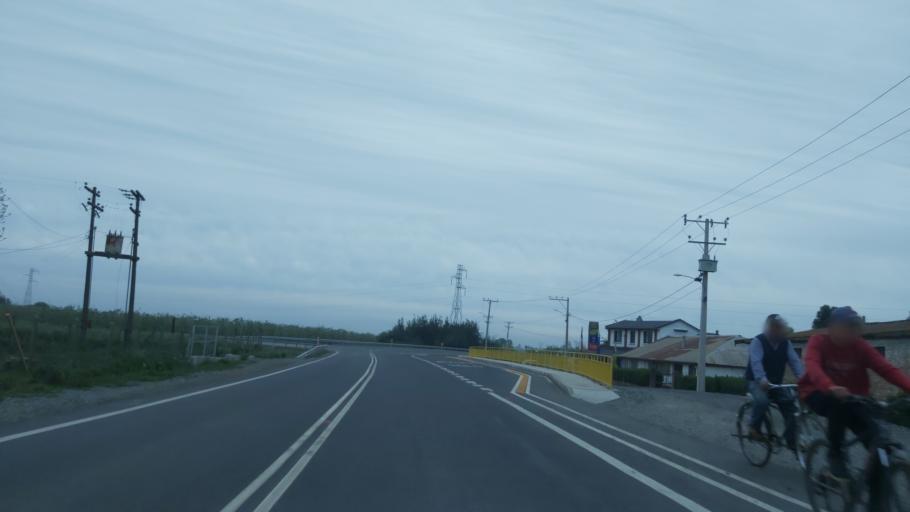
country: CL
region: Maule
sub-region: Provincia de Linares
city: Colbun
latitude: -35.6957
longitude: -71.4854
